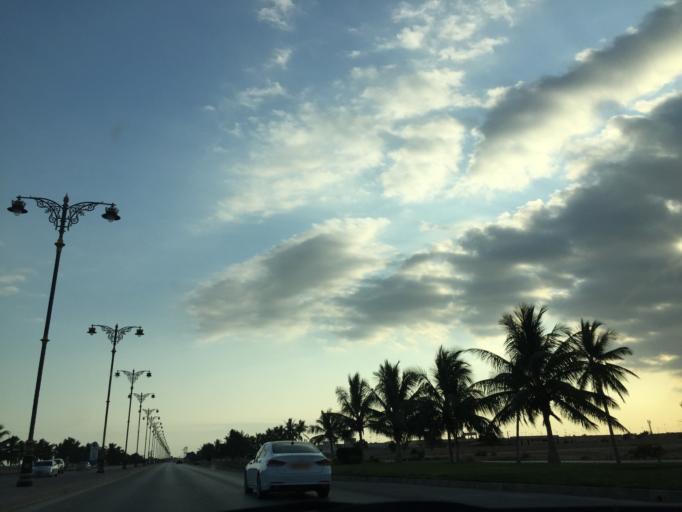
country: OM
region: Zufar
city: Salalah
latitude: 17.0445
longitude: 54.0618
